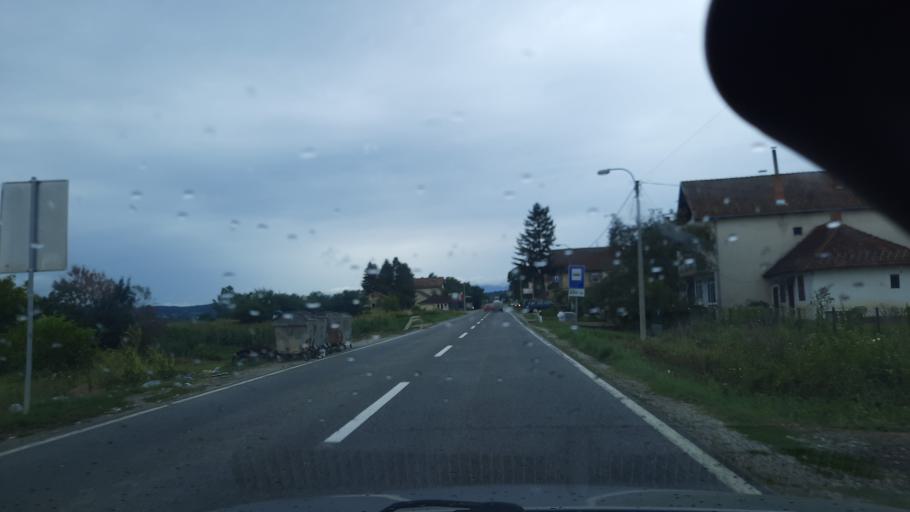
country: RS
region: Central Serbia
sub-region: Raski Okrug
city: Kraljevo
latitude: 43.7934
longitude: 20.7894
